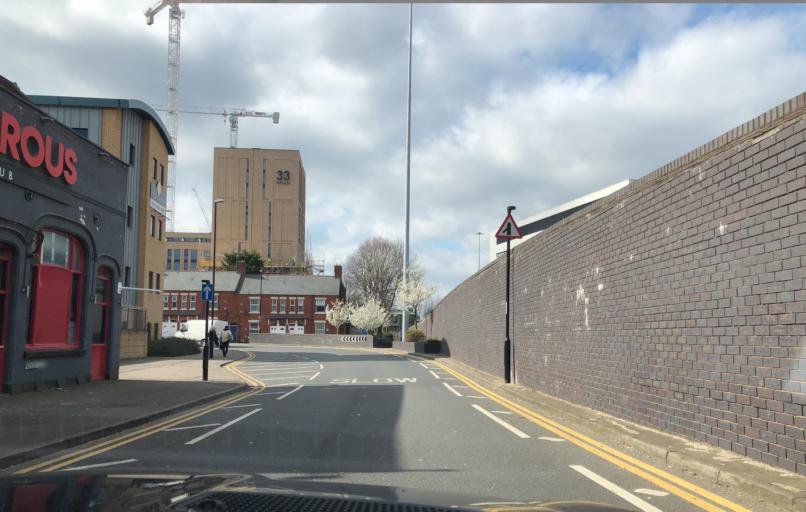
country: GB
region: England
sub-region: Coventry
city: Coventry
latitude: 52.4043
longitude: -1.5037
